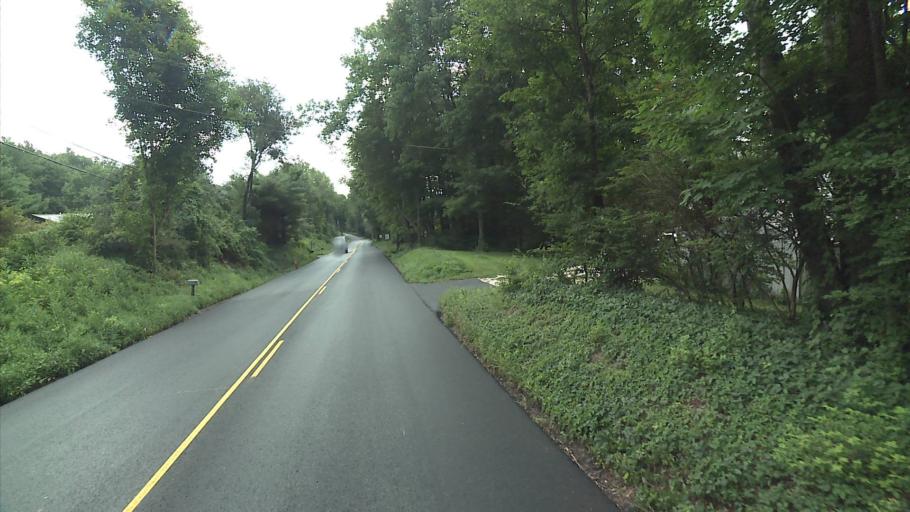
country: US
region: Connecticut
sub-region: Litchfield County
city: Canaan
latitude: 41.9828
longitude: -73.3612
